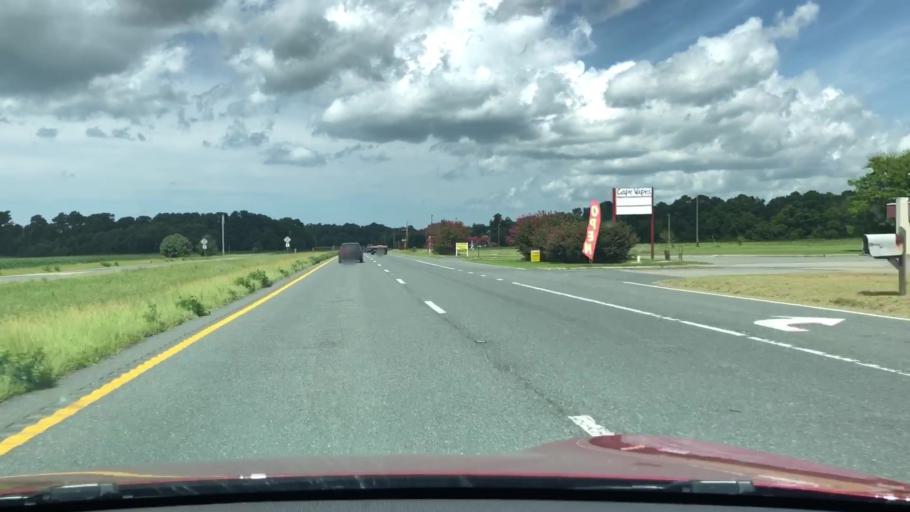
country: US
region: Virginia
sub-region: Northampton County
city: Cape Charles
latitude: 37.2772
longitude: -75.9772
